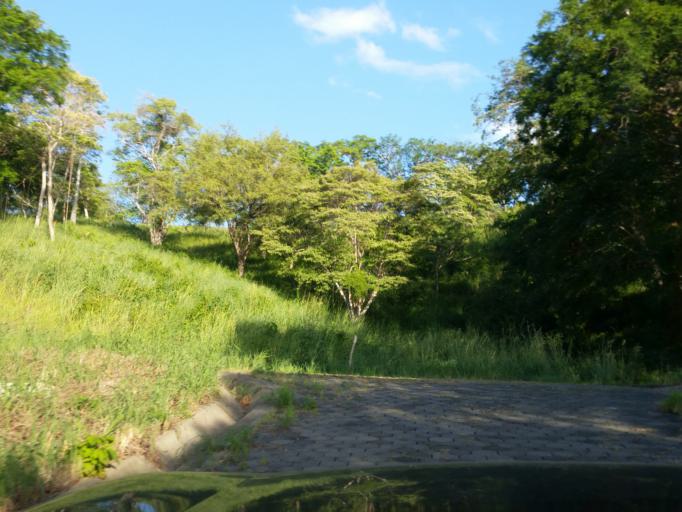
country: NI
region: Rivas
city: San Juan del Sur
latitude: 11.2409
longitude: -85.8692
